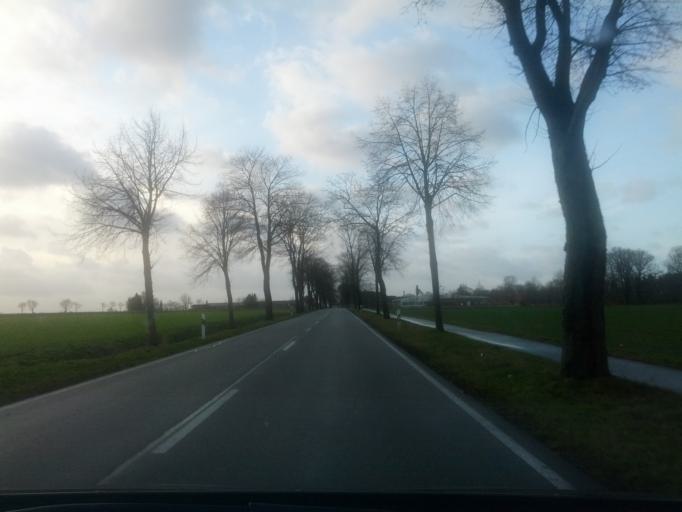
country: DE
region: Lower Saxony
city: Hamersen
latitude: 53.2619
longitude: 9.4904
